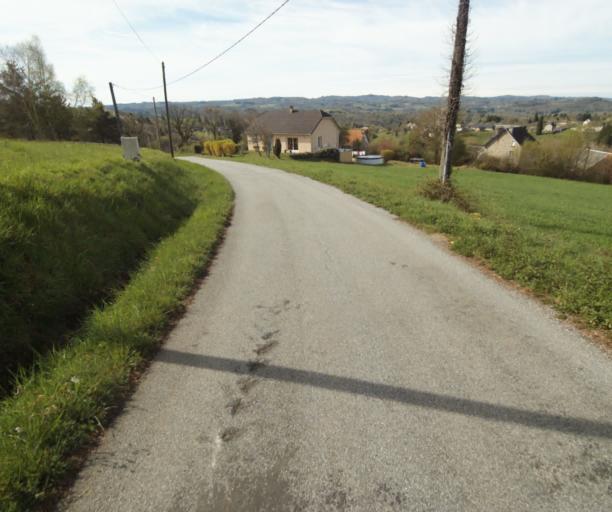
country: FR
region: Limousin
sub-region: Departement de la Correze
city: Laguenne
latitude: 45.2604
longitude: 1.8052
